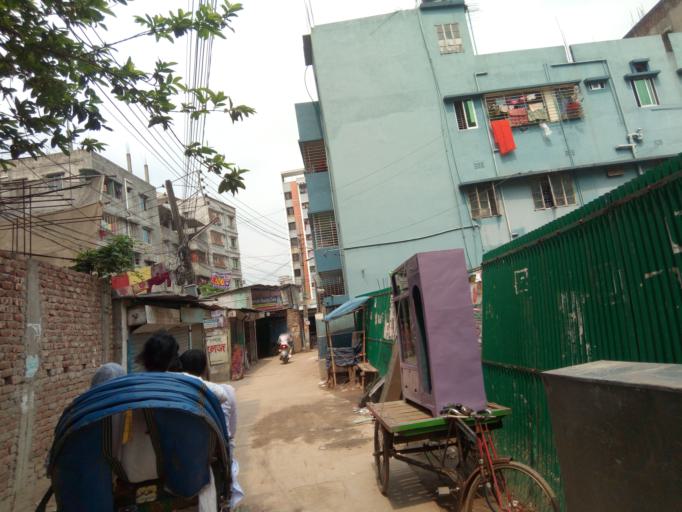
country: BD
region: Dhaka
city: Paltan
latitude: 23.7337
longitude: 90.4339
